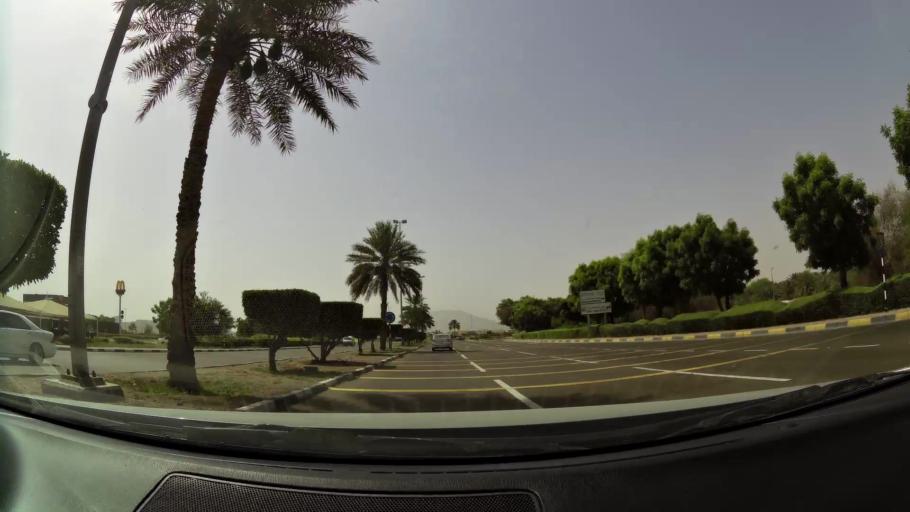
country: AE
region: Abu Dhabi
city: Al Ain
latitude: 24.1703
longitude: 55.7099
